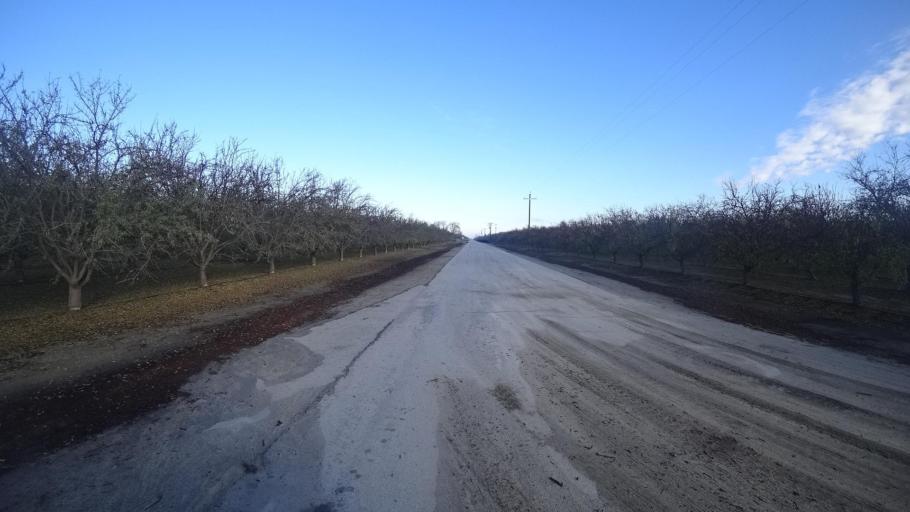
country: US
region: California
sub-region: Kern County
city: Delano
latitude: 35.7210
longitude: -119.3301
